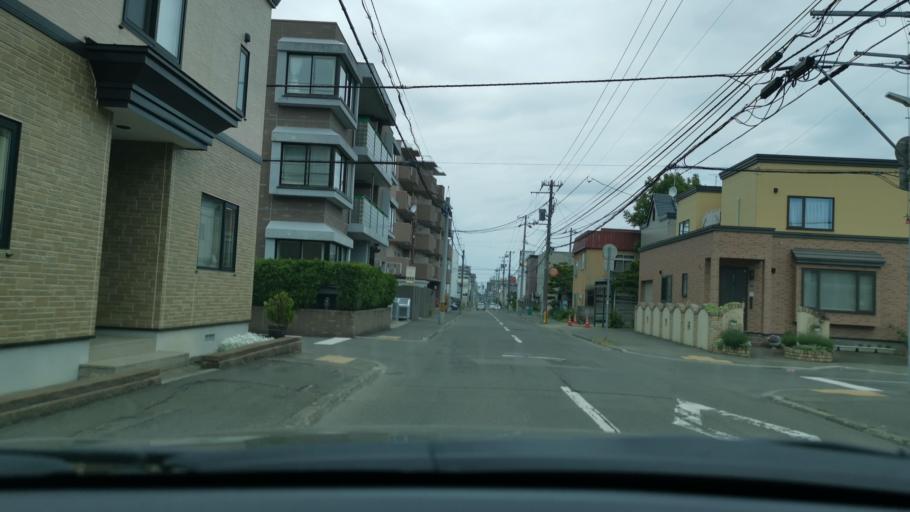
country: JP
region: Hokkaido
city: Sapporo
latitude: 43.0355
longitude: 141.3388
